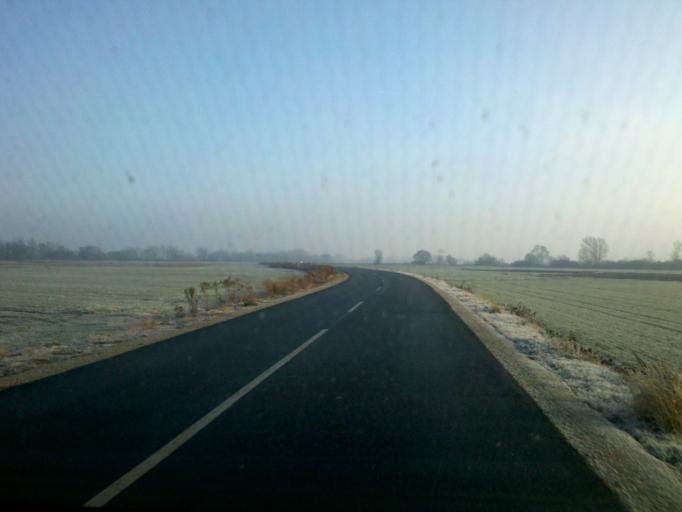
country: HR
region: Varazdinska
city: Ludbreg
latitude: 46.2631
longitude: 16.6661
